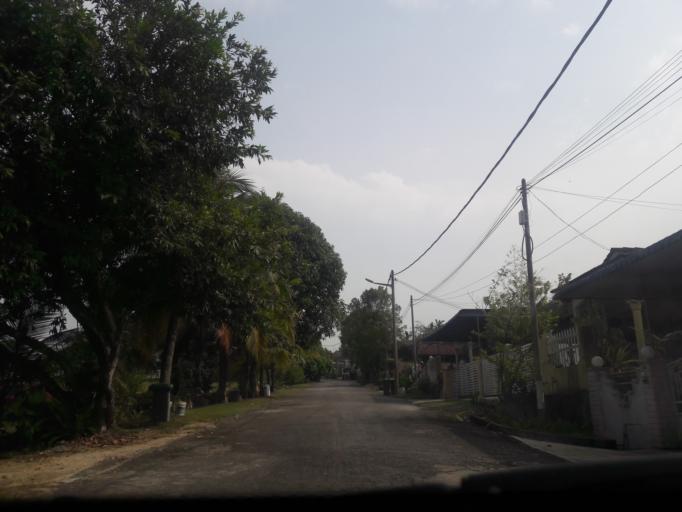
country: MY
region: Kedah
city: Kulim
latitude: 5.3583
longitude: 100.5313
